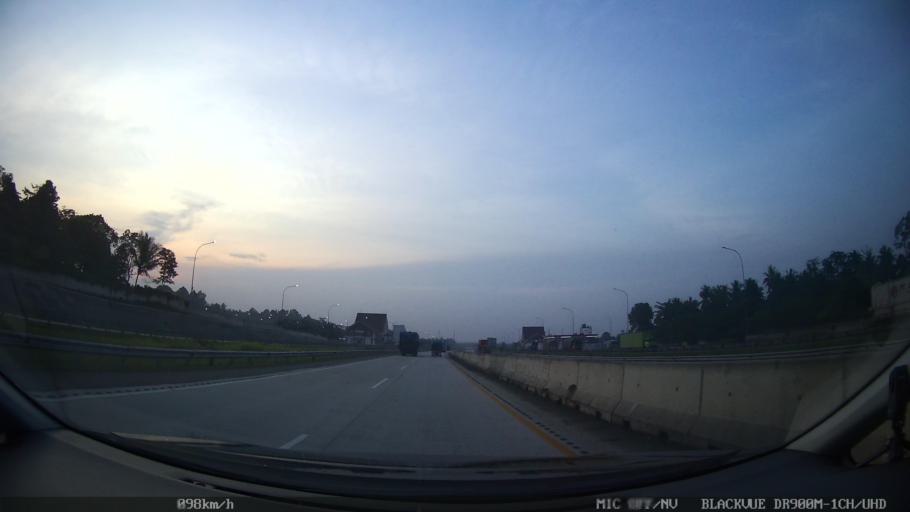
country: ID
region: Lampung
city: Pasuruan
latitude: -5.7280
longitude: 105.6708
